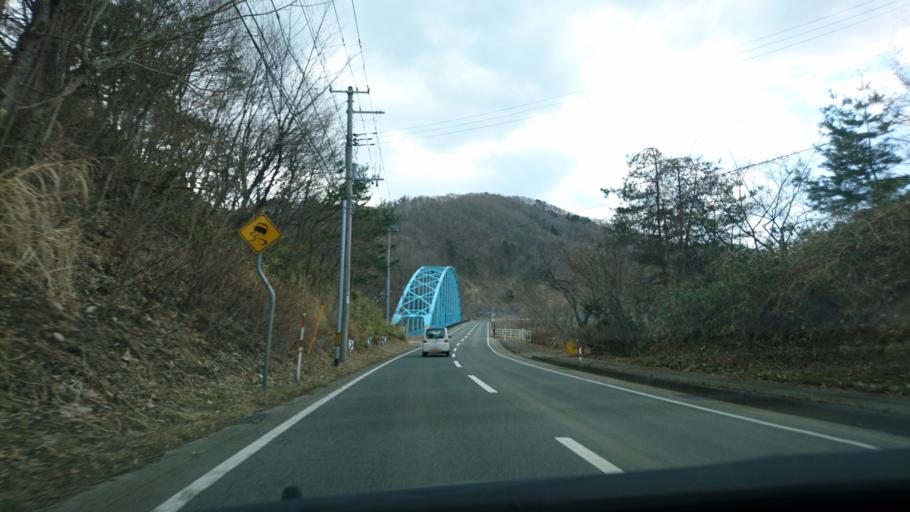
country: JP
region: Iwate
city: Shizukuishi
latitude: 39.6893
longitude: 141.0331
